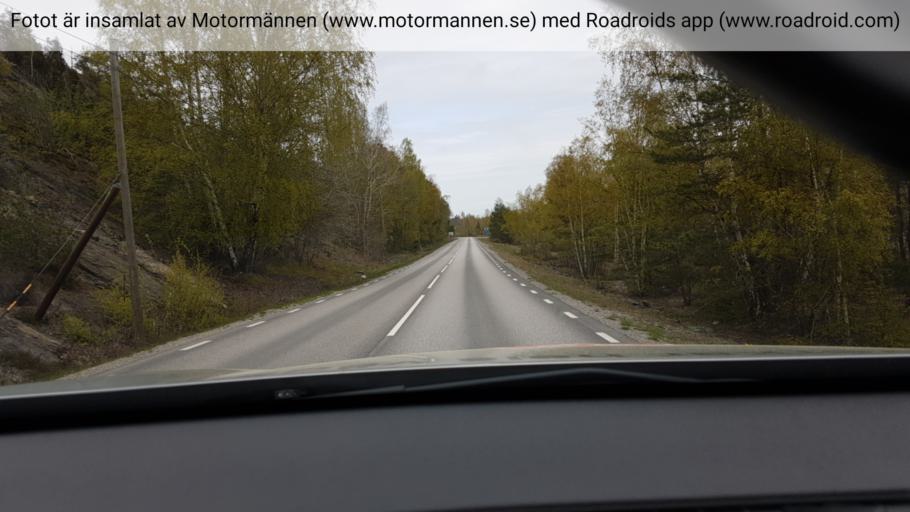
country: SE
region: Stockholm
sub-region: Nynashamns Kommun
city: Nynashamn
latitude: 58.9581
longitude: 18.0188
